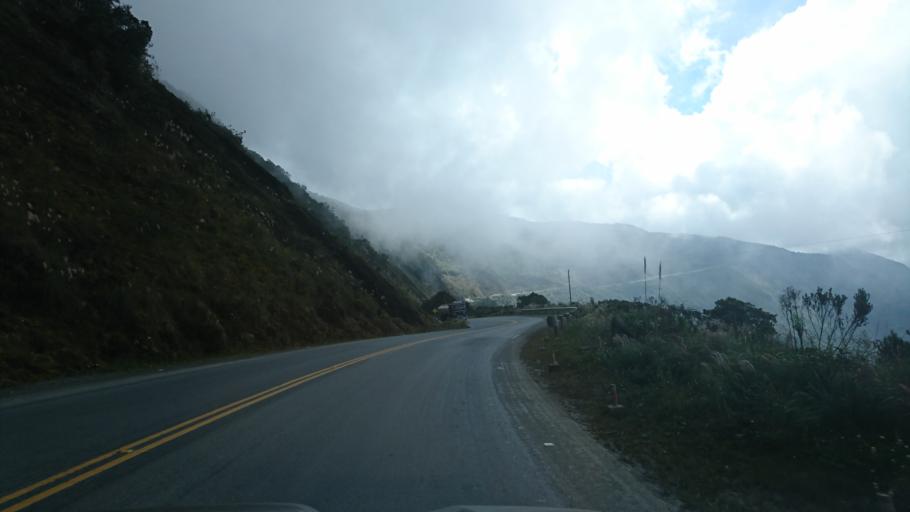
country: BO
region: La Paz
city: Coroico
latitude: -16.2975
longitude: -67.8943
